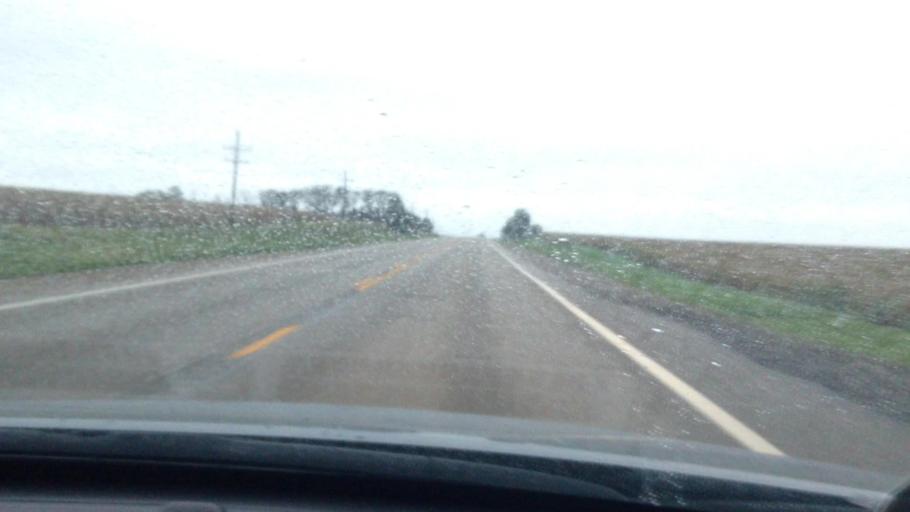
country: US
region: Kansas
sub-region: Brown County
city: Hiawatha
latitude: 39.8199
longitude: -95.5271
